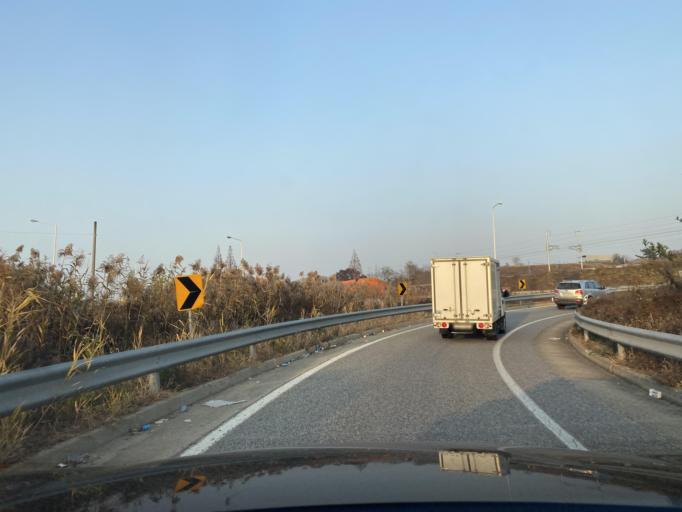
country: KR
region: Chungcheongnam-do
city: Yesan
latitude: 36.7050
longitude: 126.8305
